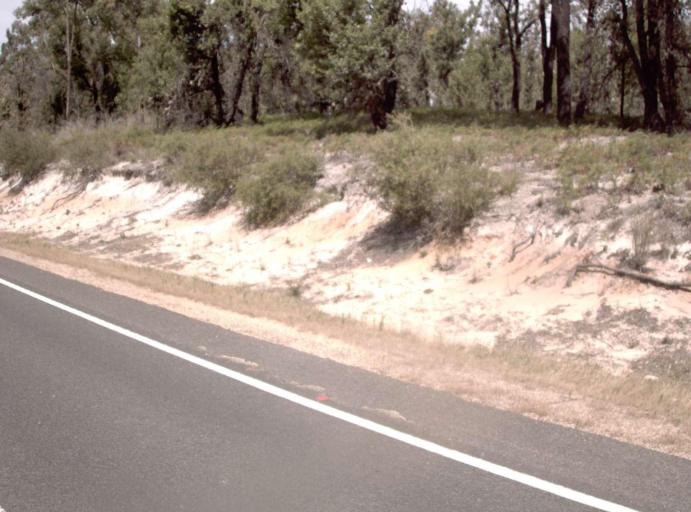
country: AU
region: Victoria
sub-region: Wellington
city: Sale
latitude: -37.9147
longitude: 147.2995
